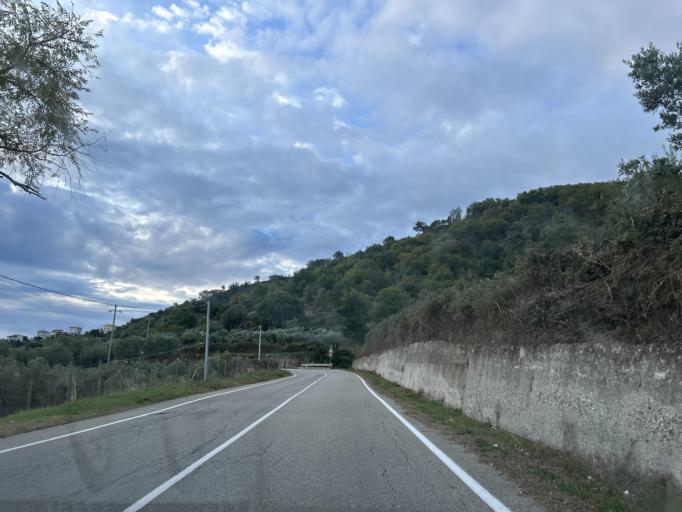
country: IT
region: Calabria
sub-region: Provincia di Catanzaro
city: Montauro
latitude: 38.7552
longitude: 16.5063
